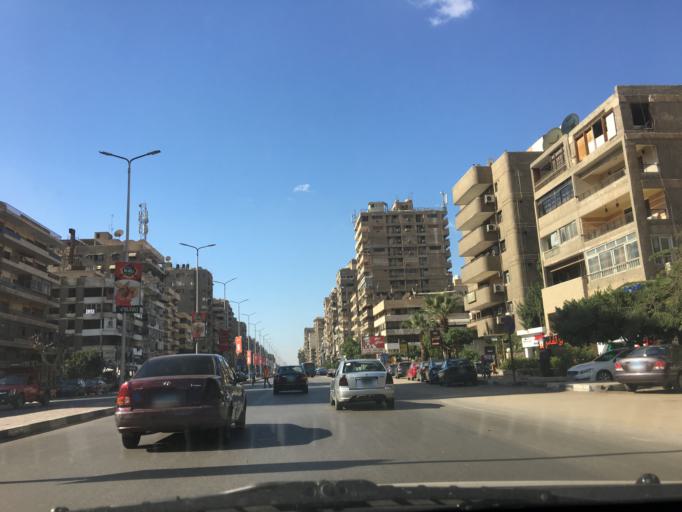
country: EG
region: Muhafazat al Qahirah
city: Cairo
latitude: 30.0544
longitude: 31.3434
